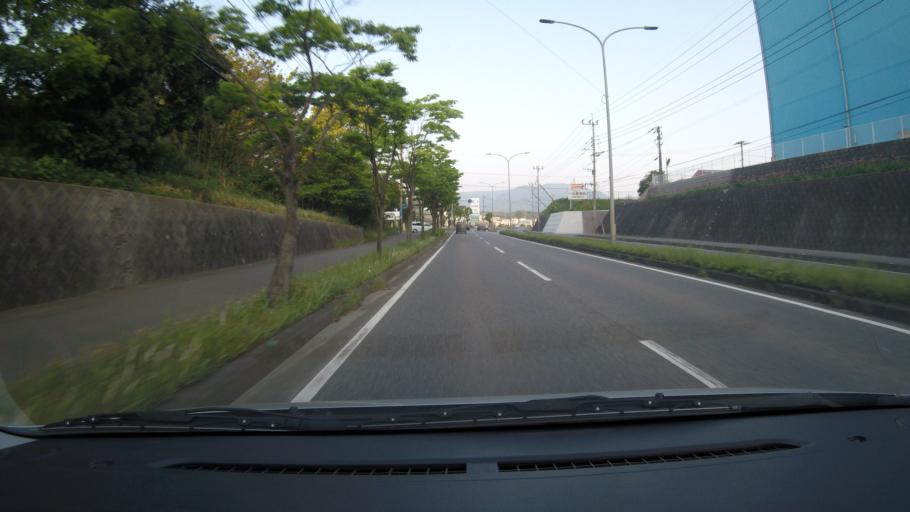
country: JP
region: Fukuoka
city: Sasaguri
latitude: 33.6484
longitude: 130.4947
